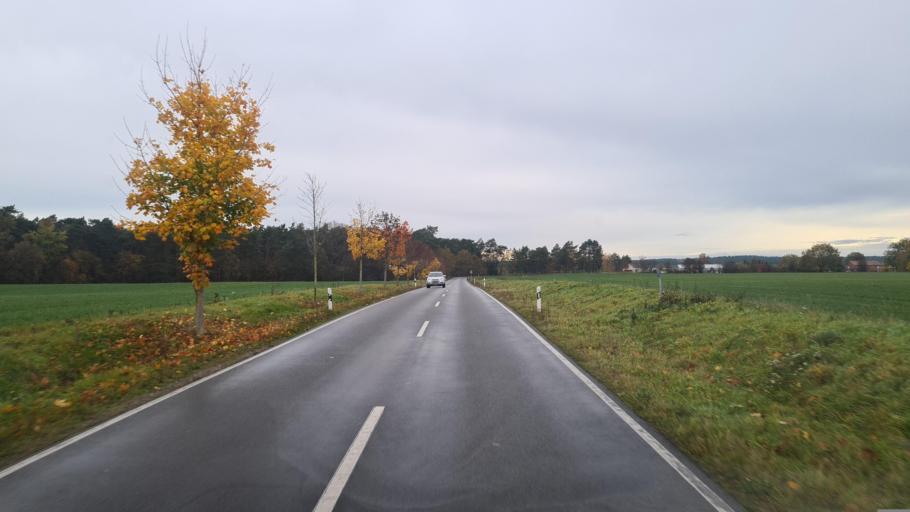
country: DE
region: Saxony-Anhalt
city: Abtsdorf
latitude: 51.9212
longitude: 12.6747
